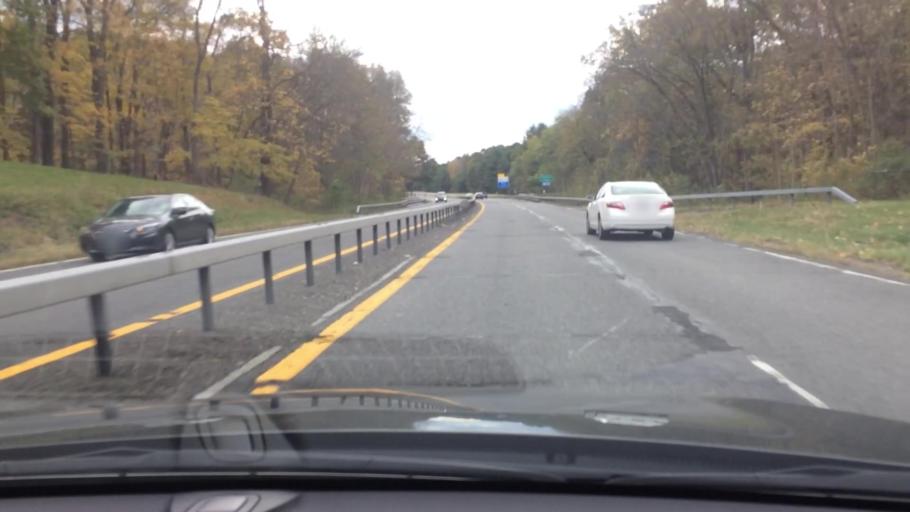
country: US
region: New York
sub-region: Dutchess County
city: Hillside Lake
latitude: 41.6671
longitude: -73.7894
